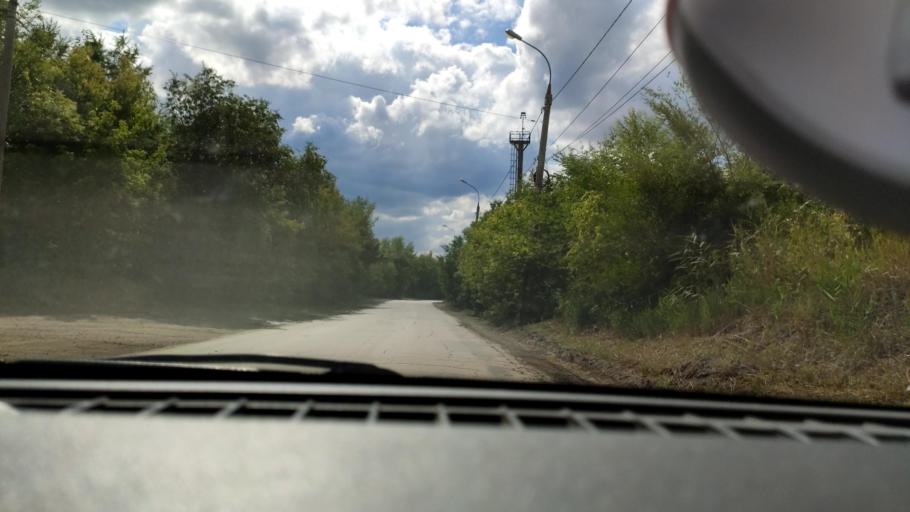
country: RU
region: Samara
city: Novokuybyshevsk
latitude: 53.1116
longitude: 50.0505
